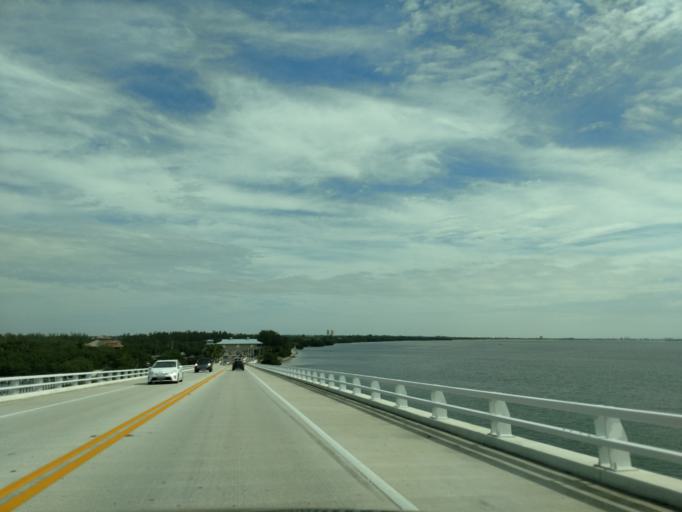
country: US
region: Florida
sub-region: Lee County
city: Punta Rassa
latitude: 26.4835
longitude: -82.0127
